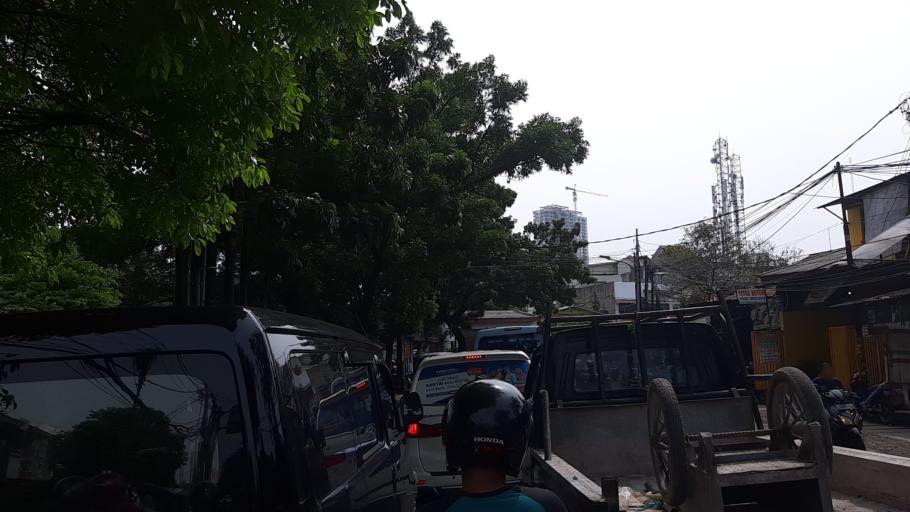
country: ID
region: Jakarta Raya
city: Jakarta
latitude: -6.2082
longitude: 106.7897
